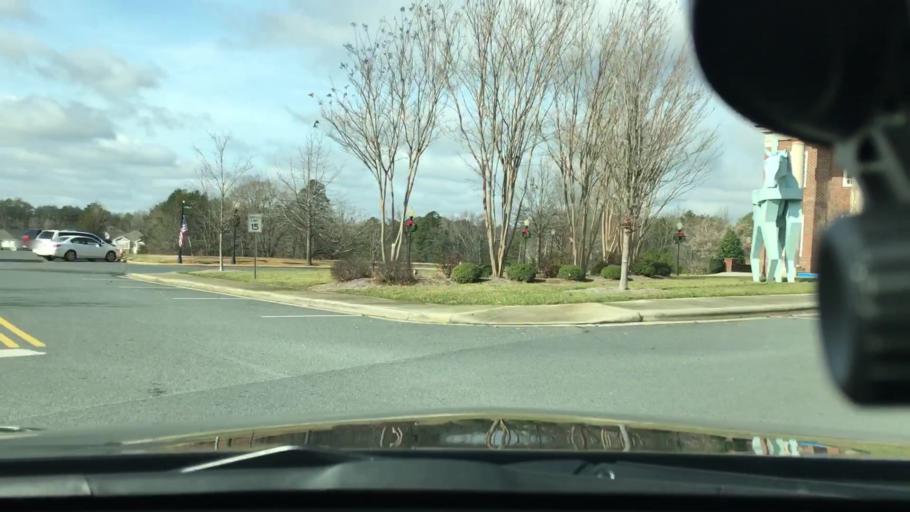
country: US
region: North Carolina
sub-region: Stanly County
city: Locust
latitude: 35.2594
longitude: -80.4312
